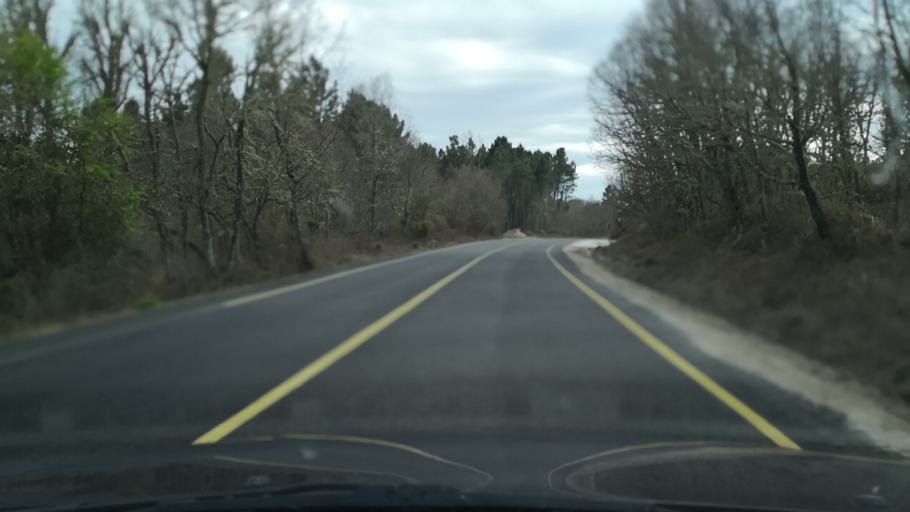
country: ES
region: Castille and Leon
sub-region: Provincia de Salamanca
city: Penaparda
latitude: 40.3043
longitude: -6.6520
